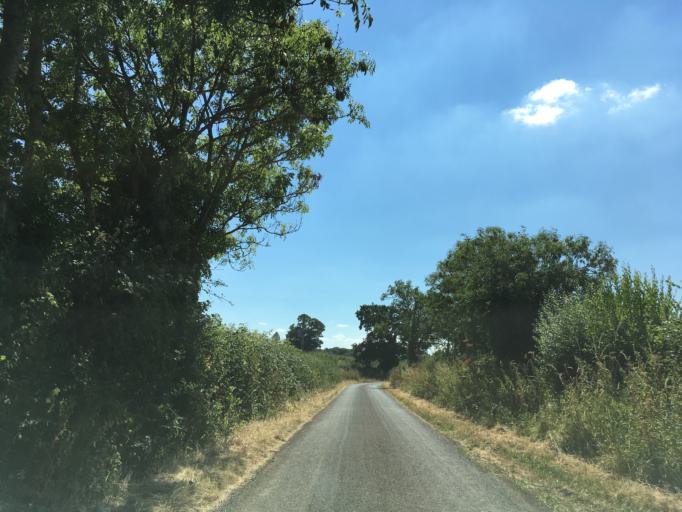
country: GB
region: England
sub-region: Wiltshire
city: Luckington
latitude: 51.5516
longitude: -2.2252
